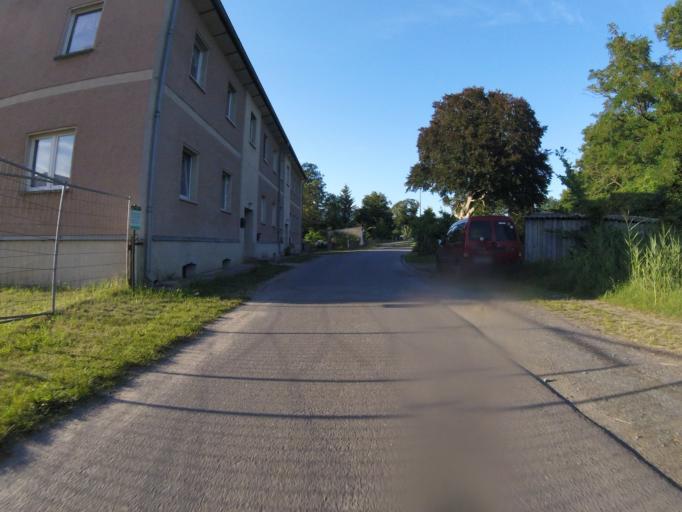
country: DE
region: Brandenburg
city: Munchehofe
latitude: 52.2166
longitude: 13.7742
